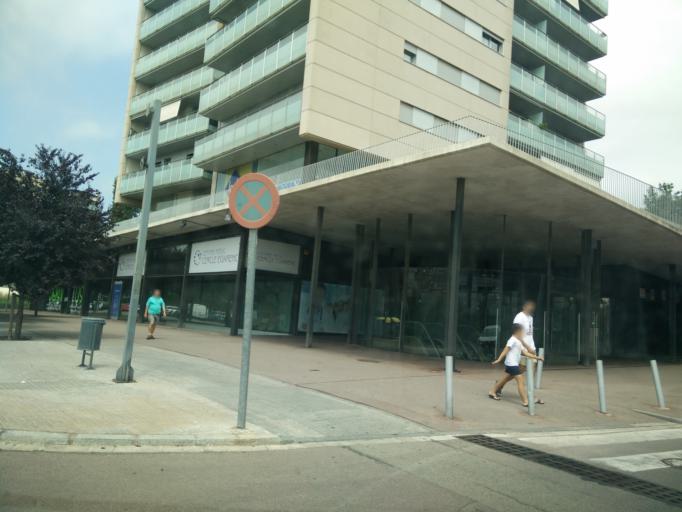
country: ES
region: Catalonia
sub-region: Provincia de Barcelona
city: Terrassa
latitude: 41.5702
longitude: 2.0144
